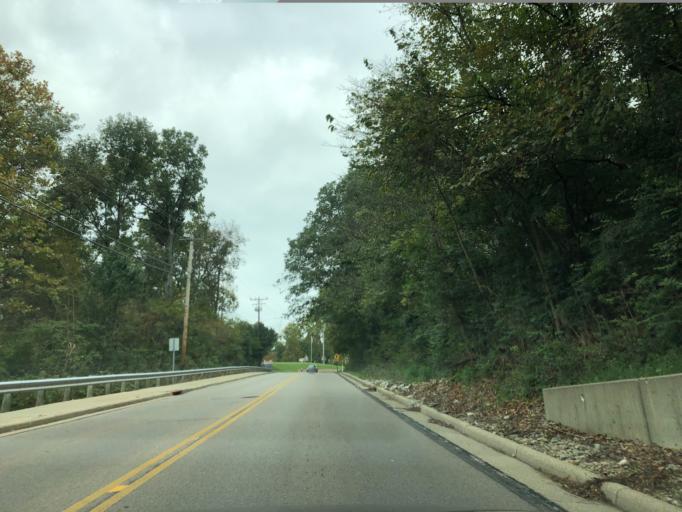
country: US
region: Ohio
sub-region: Hamilton County
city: The Village of Indian Hill
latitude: 39.2584
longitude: -84.2885
